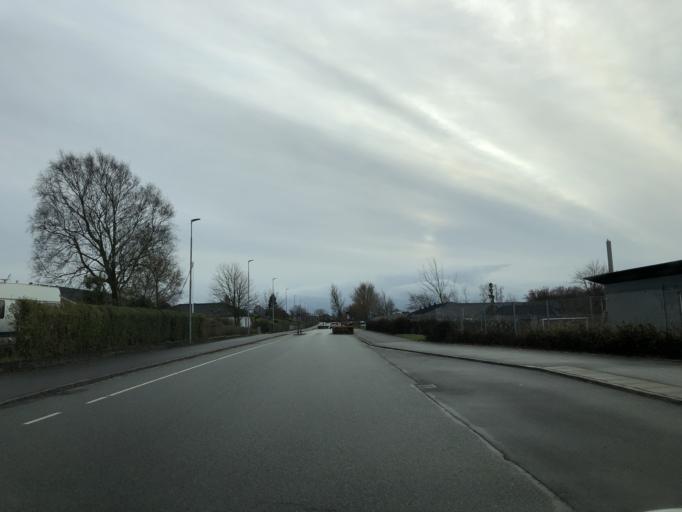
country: DK
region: Central Jutland
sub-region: Struer Kommune
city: Struer
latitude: 56.4874
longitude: 8.5752
